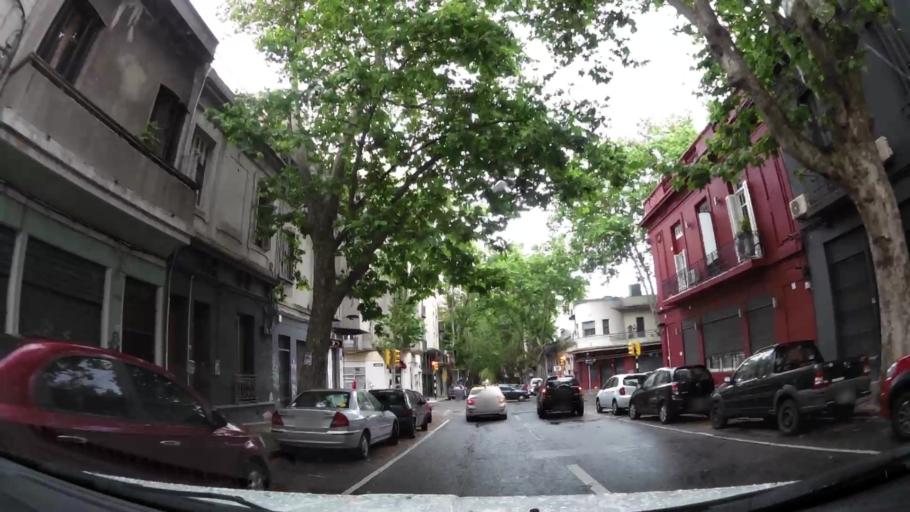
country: UY
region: Montevideo
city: Montevideo
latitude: -34.9090
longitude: -56.1952
